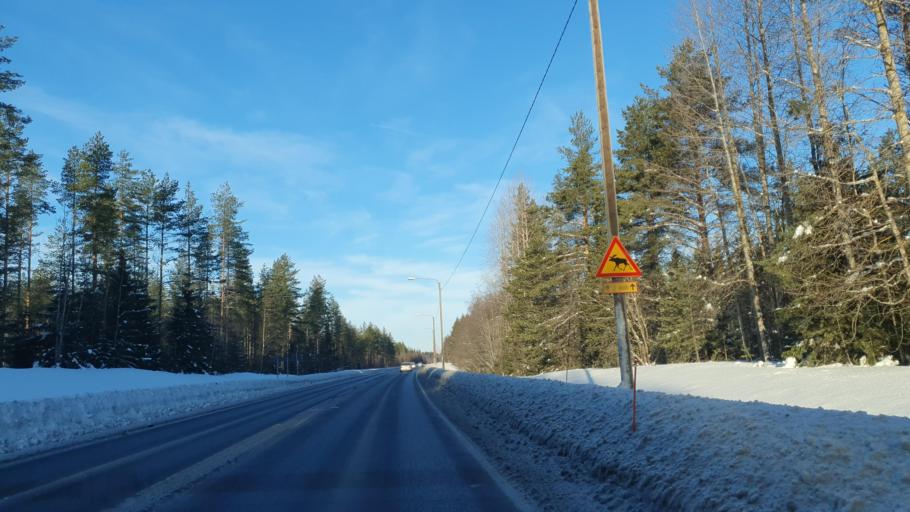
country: FI
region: Northern Ostrobothnia
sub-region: Oulu
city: Tyrnaevae
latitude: 64.9351
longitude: 25.7128
